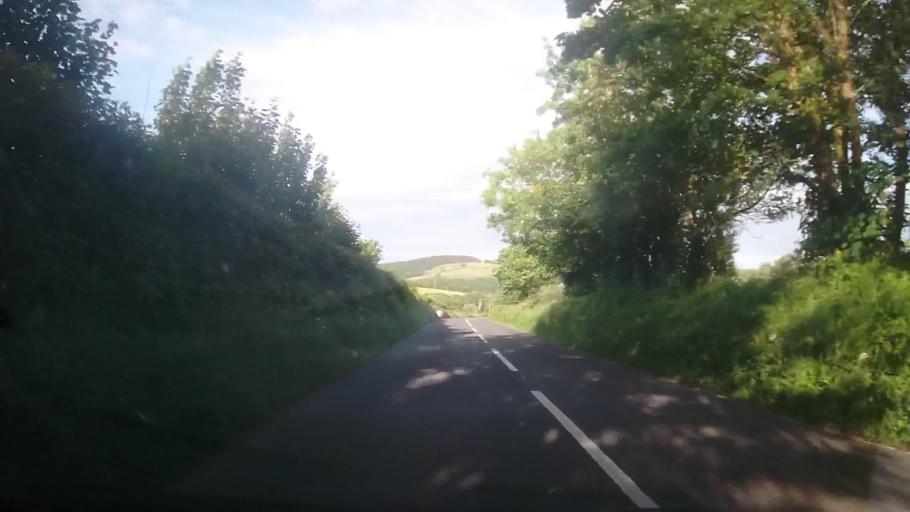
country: GB
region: England
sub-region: Devon
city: Ivybridge
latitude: 50.3526
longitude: -3.9372
